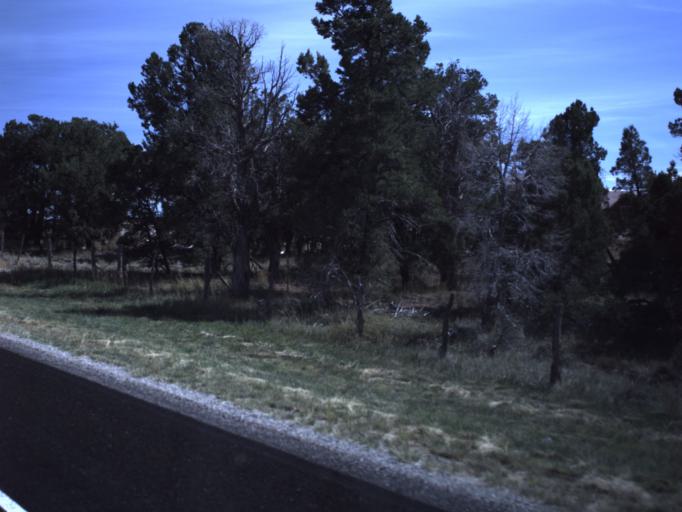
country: US
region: Utah
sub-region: San Juan County
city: Monticello
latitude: 37.8567
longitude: -109.1931
